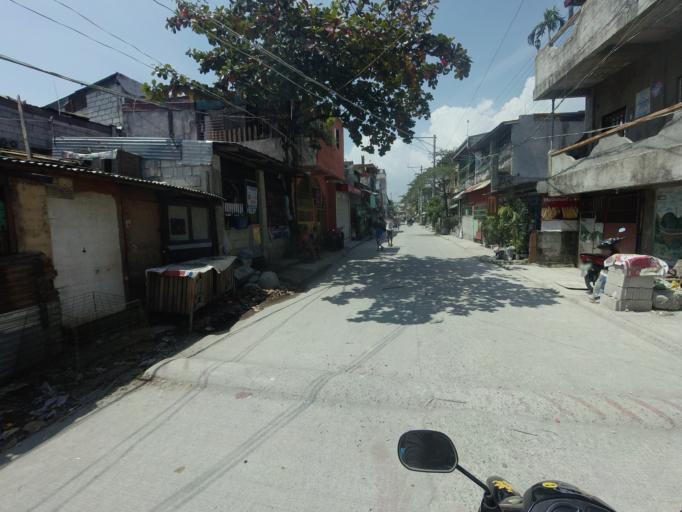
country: PH
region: Calabarzon
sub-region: Province of Rizal
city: Taguig
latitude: 14.5388
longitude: 121.1071
